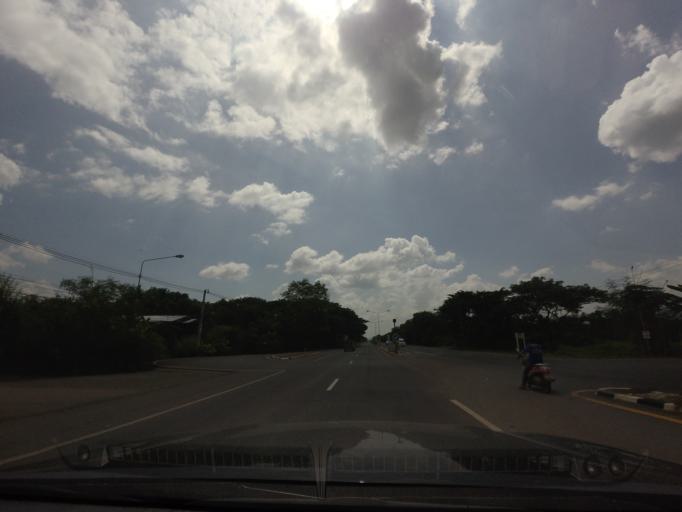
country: TH
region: Phetchabun
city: Nong Phai
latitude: 16.1615
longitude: 101.0700
